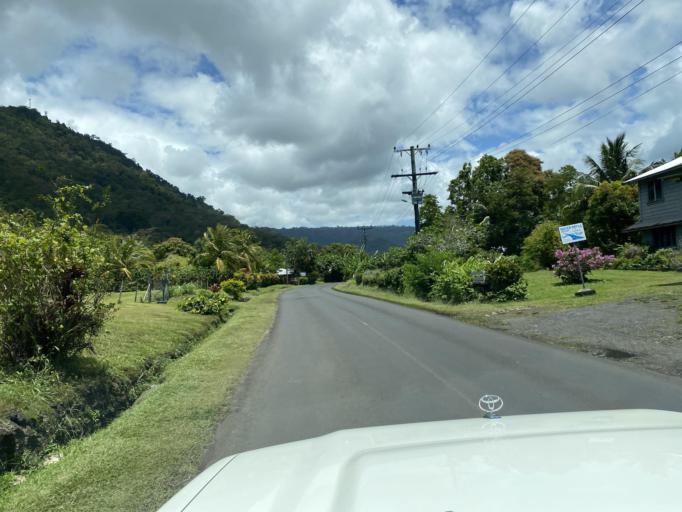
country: WS
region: Tuamasaga
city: Apia
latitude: -13.8456
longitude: -171.7773
